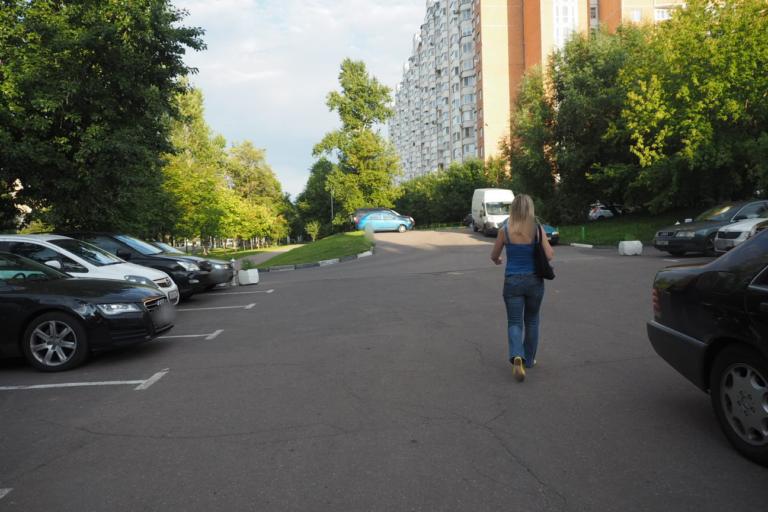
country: RU
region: Moskovskaya
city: Cheremushki
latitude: 55.6730
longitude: 37.5758
